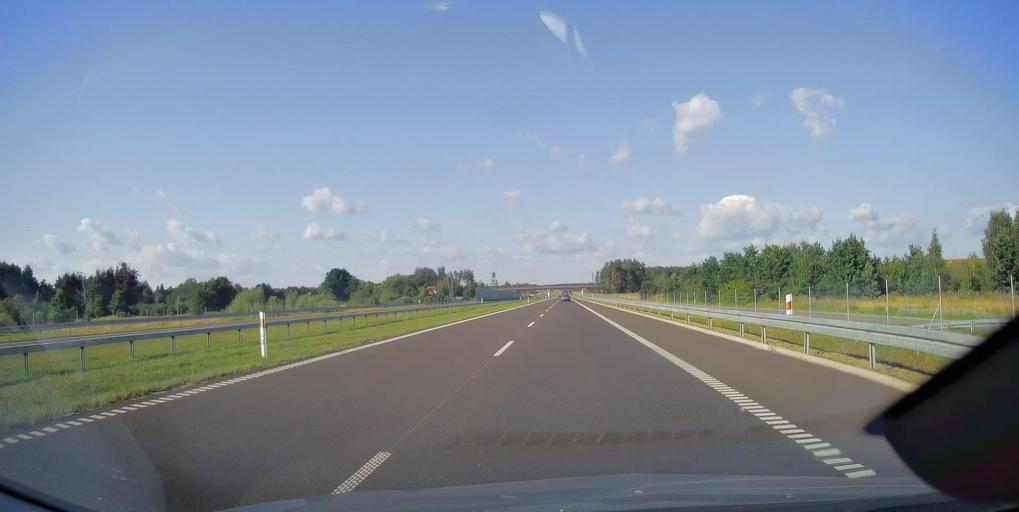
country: PL
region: Masovian Voivodeship
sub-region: Powiat radomski
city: Jedlinsk
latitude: 51.4845
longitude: 21.0667
